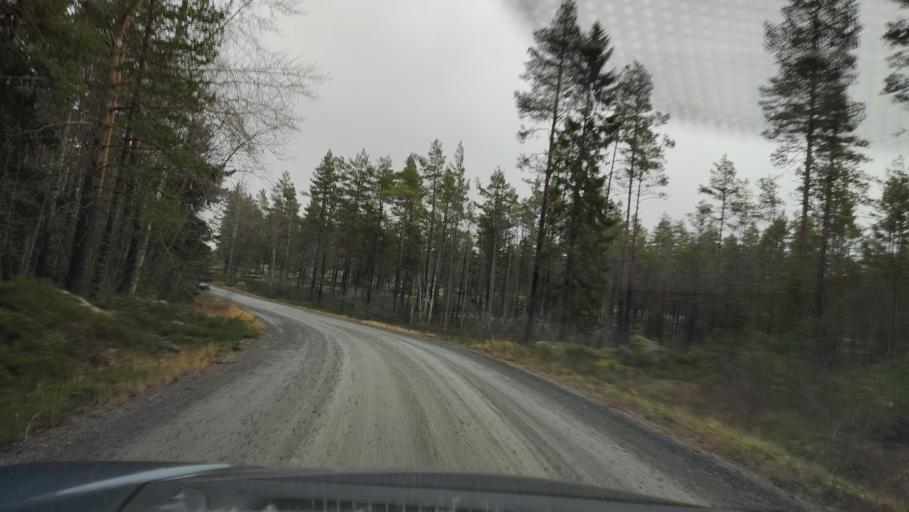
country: FI
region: Southern Ostrobothnia
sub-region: Suupohja
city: Karijoki
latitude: 62.1381
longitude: 21.6502
